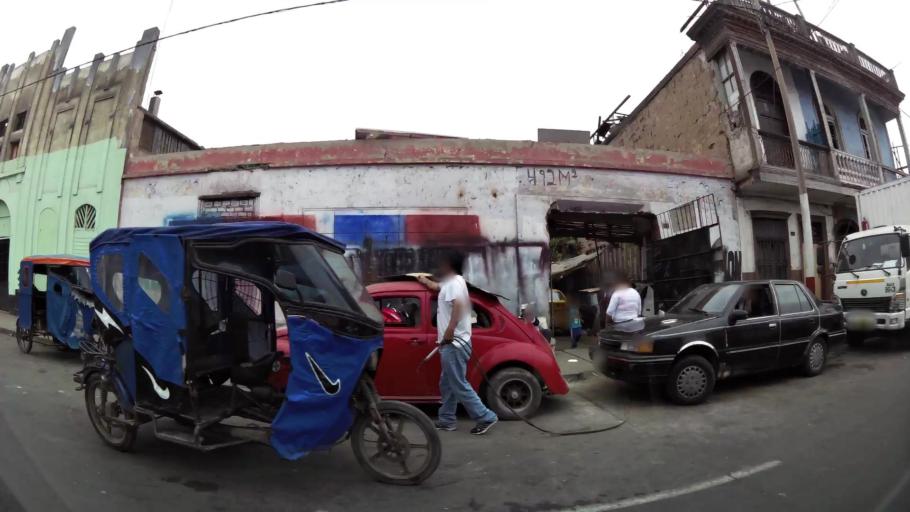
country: PE
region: Callao
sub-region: Callao
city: Callao
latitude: -12.0632
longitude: -77.1433
